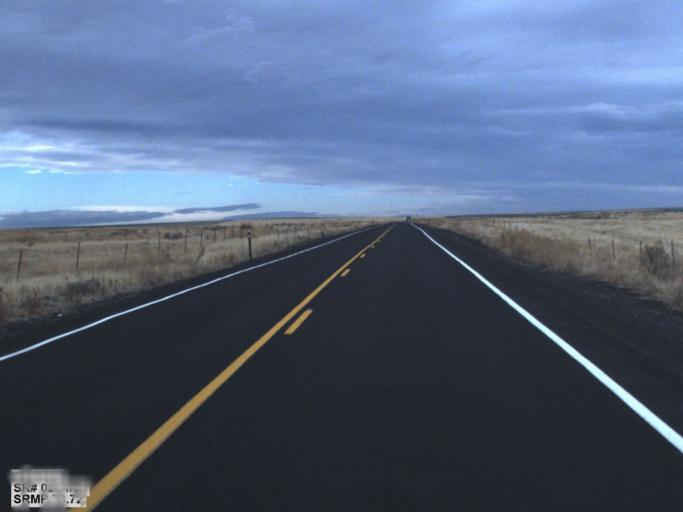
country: US
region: Washington
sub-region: Okanogan County
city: Coulee Dam
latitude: 47.5485
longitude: -118.7855
